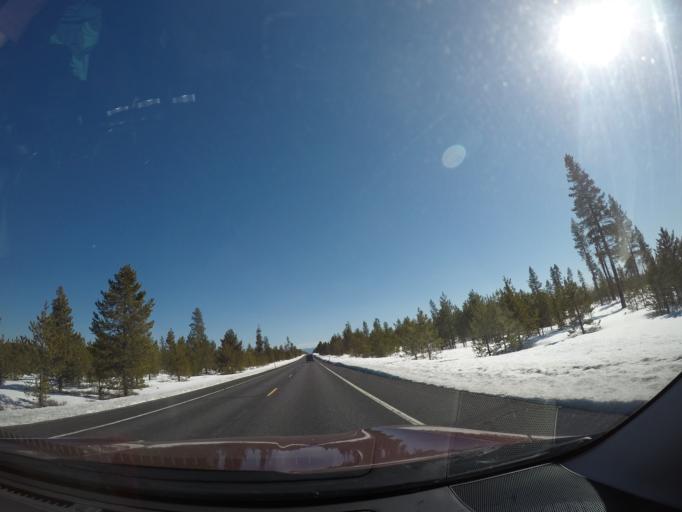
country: US
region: Oregon
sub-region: Deschutes County
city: Three Rivers
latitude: 43.8820
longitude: -121.5702
